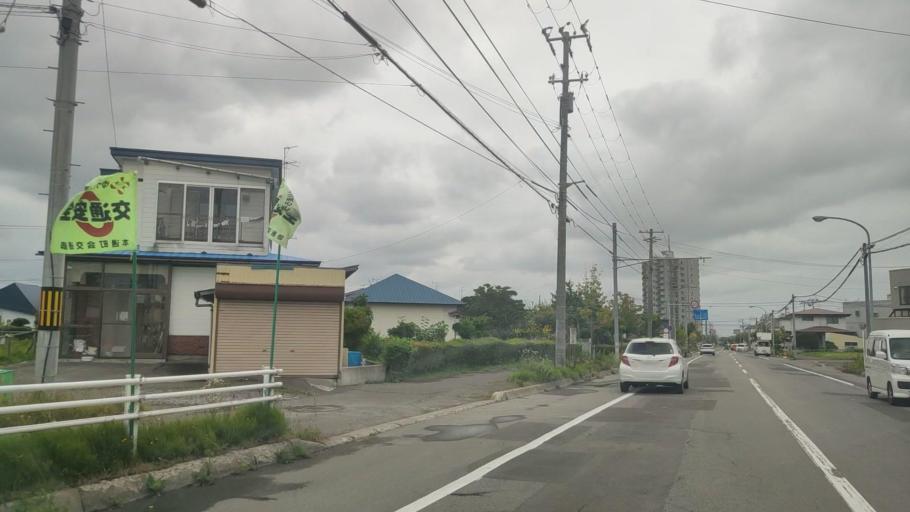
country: JP
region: Hokkaido
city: Hakodate
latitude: 41.7995
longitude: 140.7603
